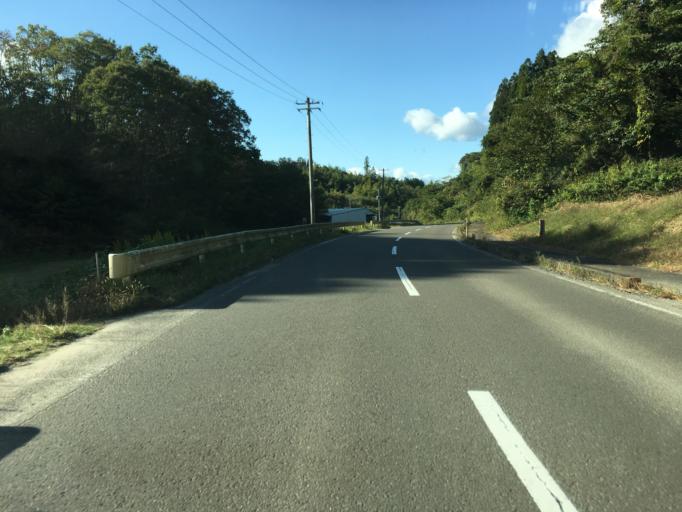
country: JP
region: Miyagi
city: Marumori
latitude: 37.8596
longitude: 140.8291
